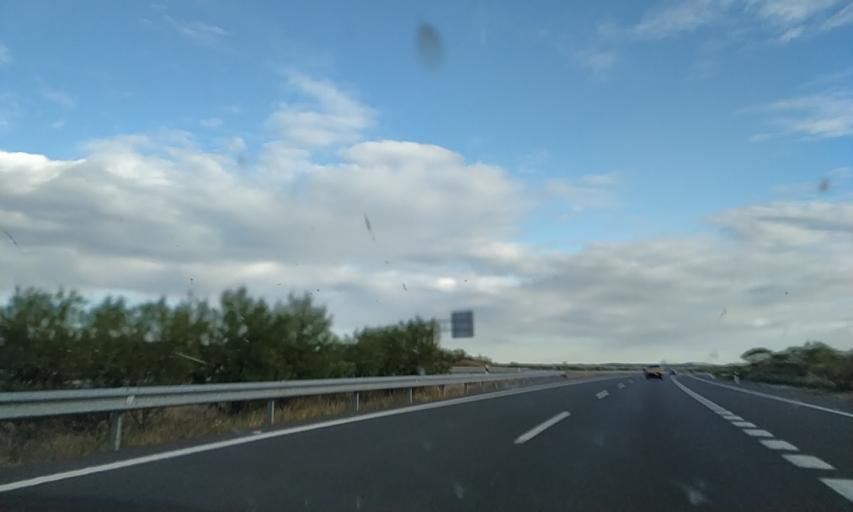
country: ES
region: Extremadura
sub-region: Provincia de Caceres
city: Hinojal
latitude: 39.6936
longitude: -6.3995
